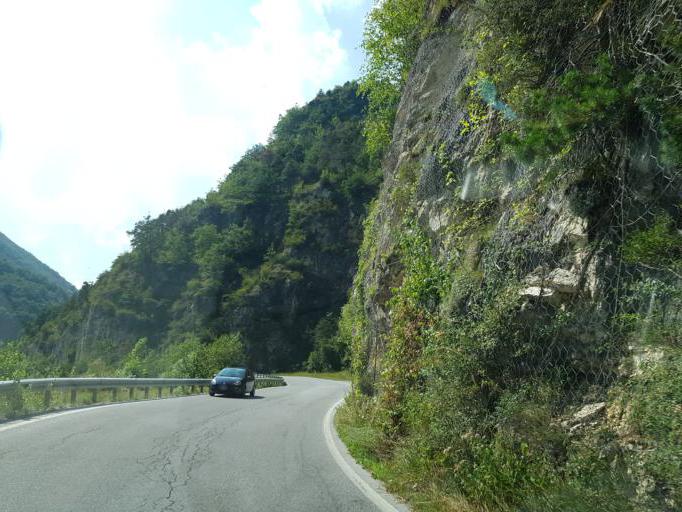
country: IT
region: Piedmont
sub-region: Provincia di Cuneo
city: Macra
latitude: 44.4961
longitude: 7.2029
